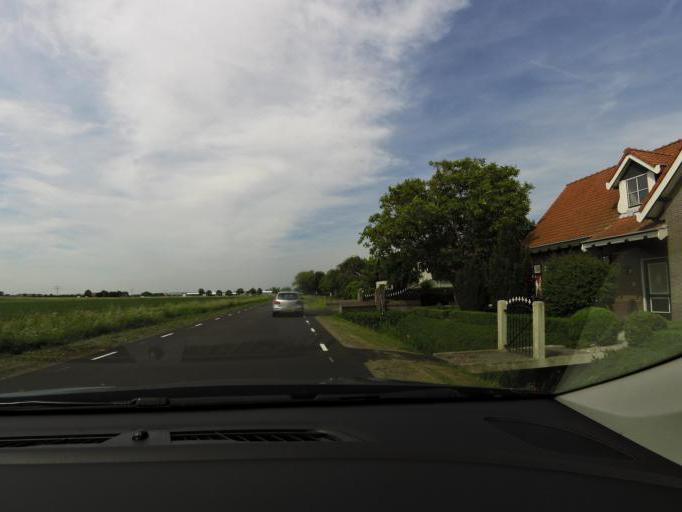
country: NL
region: North Brabant
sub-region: Gemeente Moerdijk
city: Willemstad
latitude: 51.7475
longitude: 4.4214
